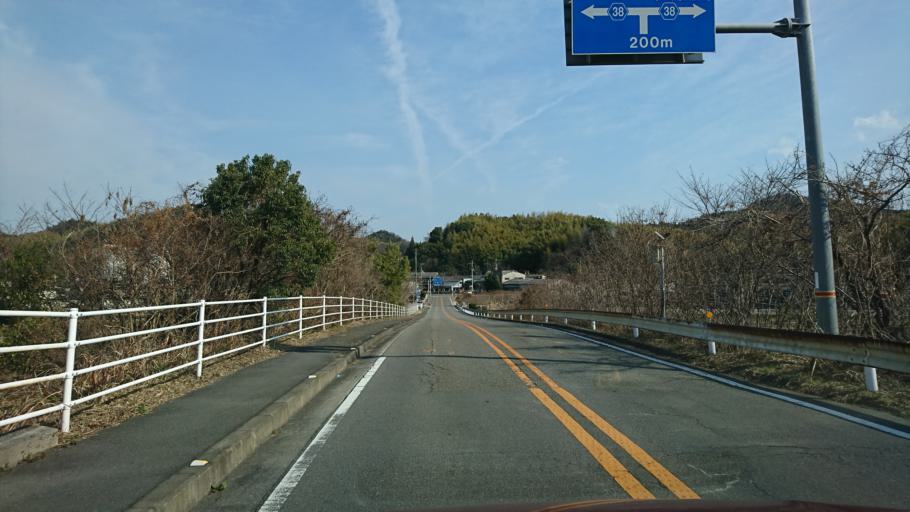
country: JP
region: Ehime
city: Saijo
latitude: 34.0062
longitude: 133.0362
